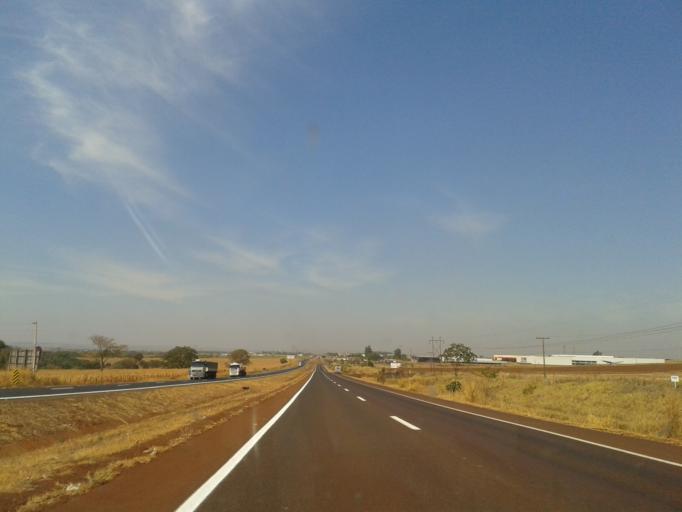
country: BR
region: Goias
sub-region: Itumbiara
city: Itumbiara
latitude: -18.3123
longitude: -49.2317
